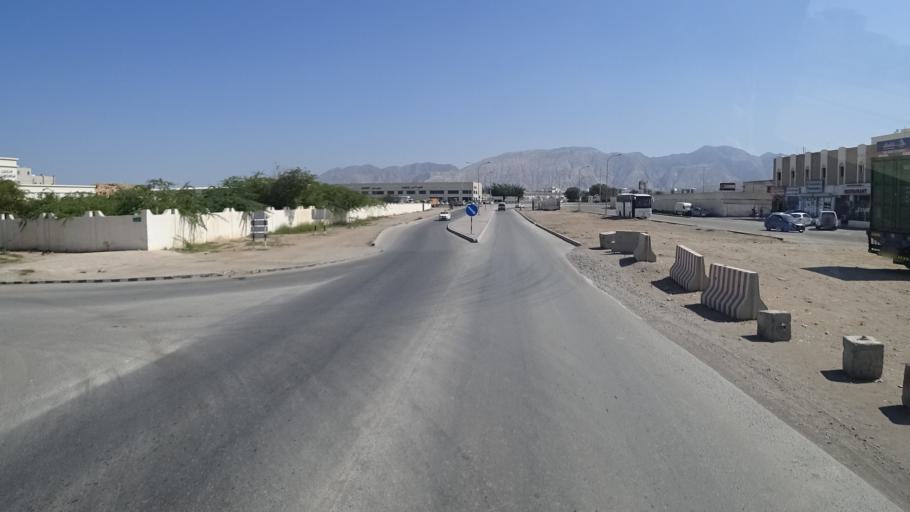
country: OM
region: Muhafazat Masqat
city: Bawshar
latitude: 23.5720
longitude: 58.3786
